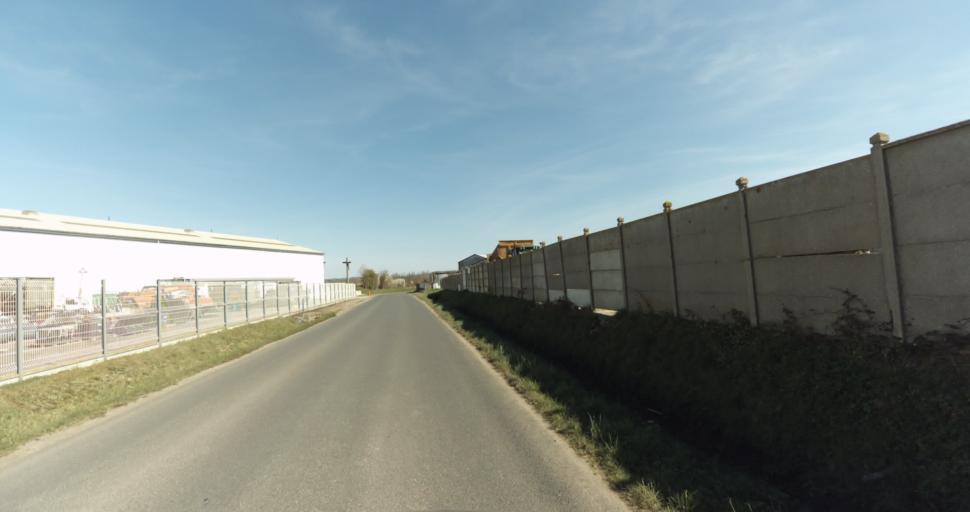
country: FR
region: Lower Normandy
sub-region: Departement du Calvados
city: Saint-Pierre-sur-Dives
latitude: 49.0251
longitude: -0.0446
